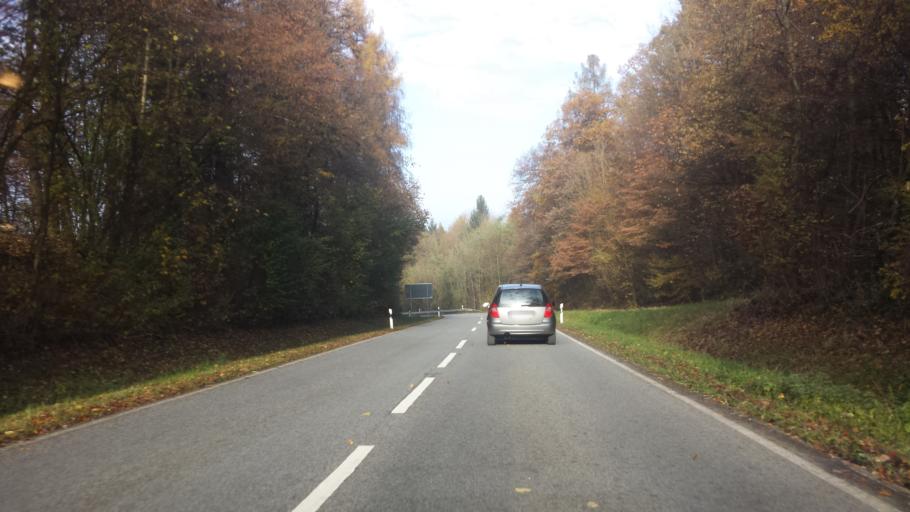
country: DE
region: Baden-Wuerttemberg
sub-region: Karlsruhe Region
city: Obrigheim
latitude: 49.3286
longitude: 9.0663
